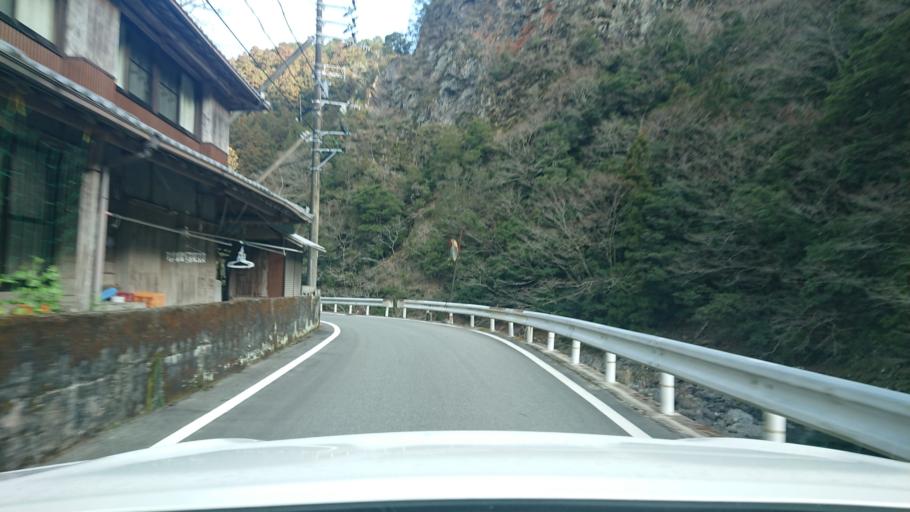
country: JP
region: Tokushima
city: Ishii
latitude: 33.8991
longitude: 134.3972
